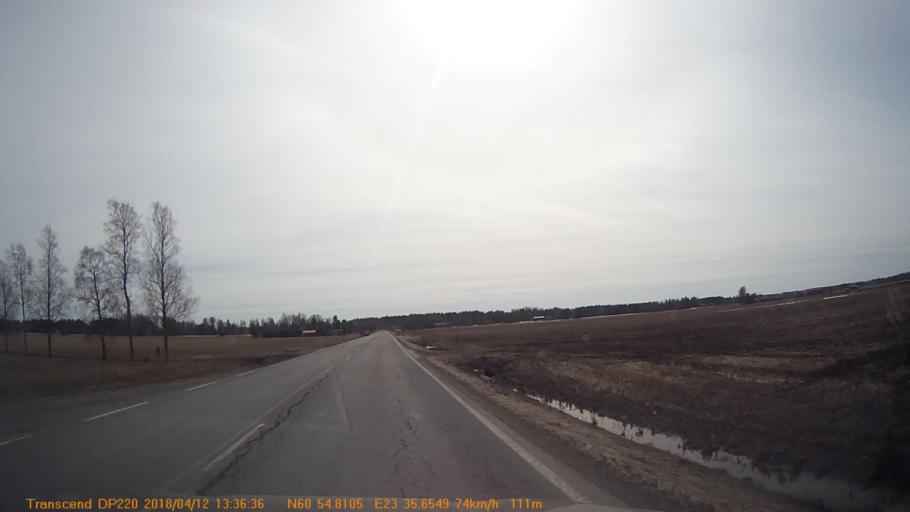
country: FI
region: Haeme
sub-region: Forssa
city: Forssa
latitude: 60.9133
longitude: 23.5942
